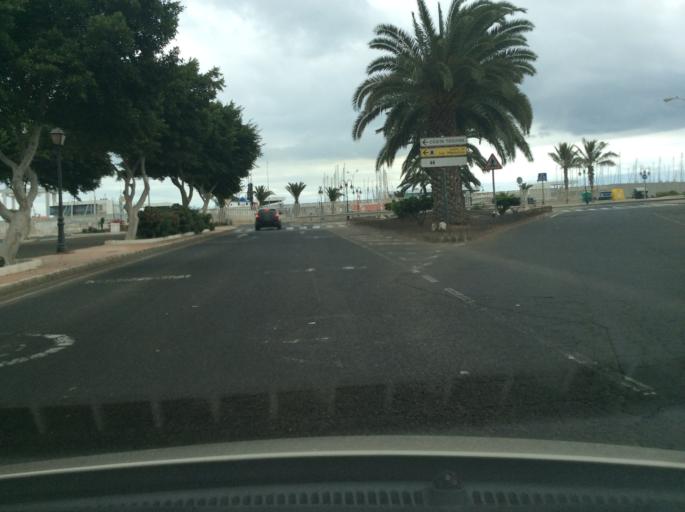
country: ES
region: Canary Islands
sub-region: Provincia de Las Palmas
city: Arrecife
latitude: 28.9657
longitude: -13.5411
